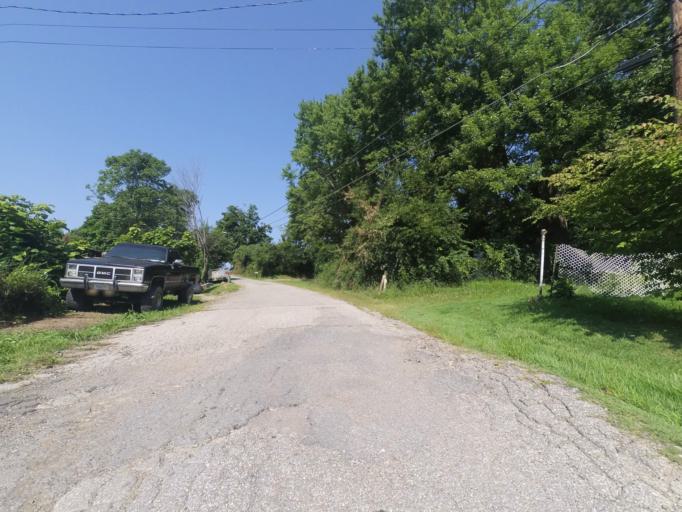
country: US
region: West Virginia
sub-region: Cabell County
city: Huntington
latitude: 38.4372
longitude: -82.4395
